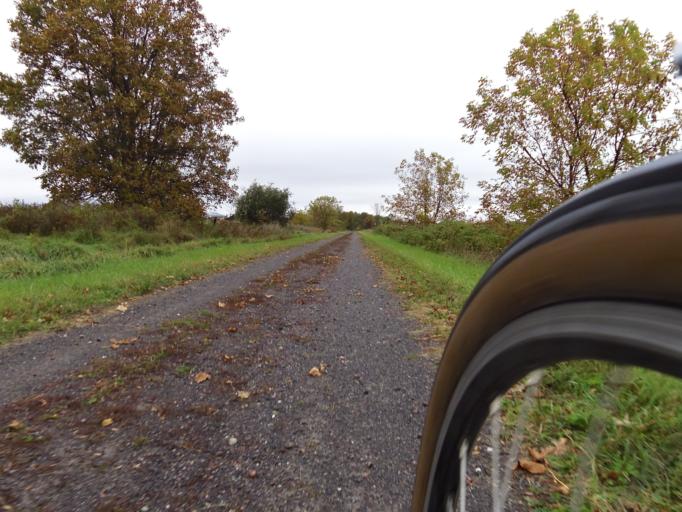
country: CA
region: Quebec
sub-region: Outaouais
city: Shawville
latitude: 45.7103
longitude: -76.5894
